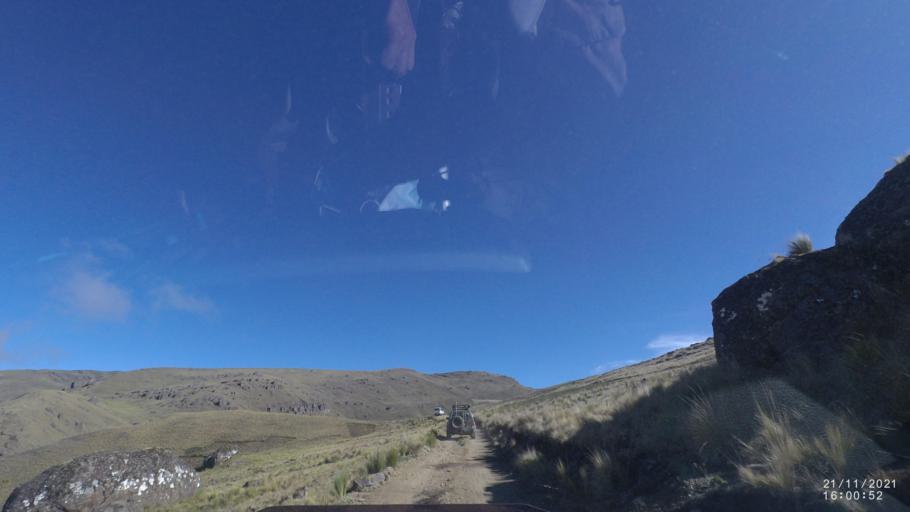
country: BO
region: Cochabamba
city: Cochabamba
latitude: -16.9822
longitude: -66.2617
